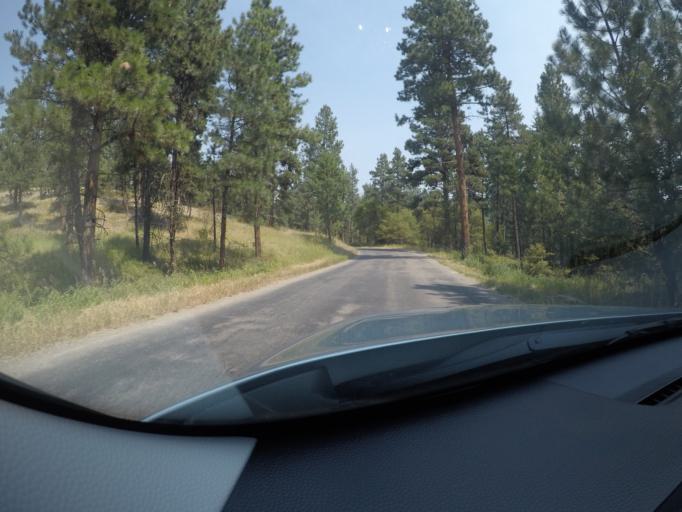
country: US
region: Montana
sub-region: Lake County
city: Polson
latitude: 47.7640
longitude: -114.1579
